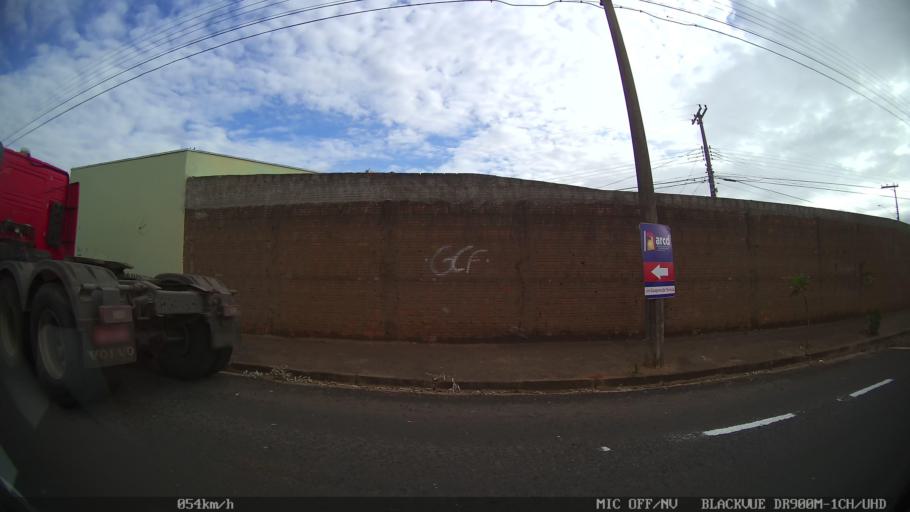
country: BR
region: Sao Paulo
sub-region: Sao Jose Do Rio Preto
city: Sao Jose do Rio Preto
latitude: -20.8263
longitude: -49.4125
